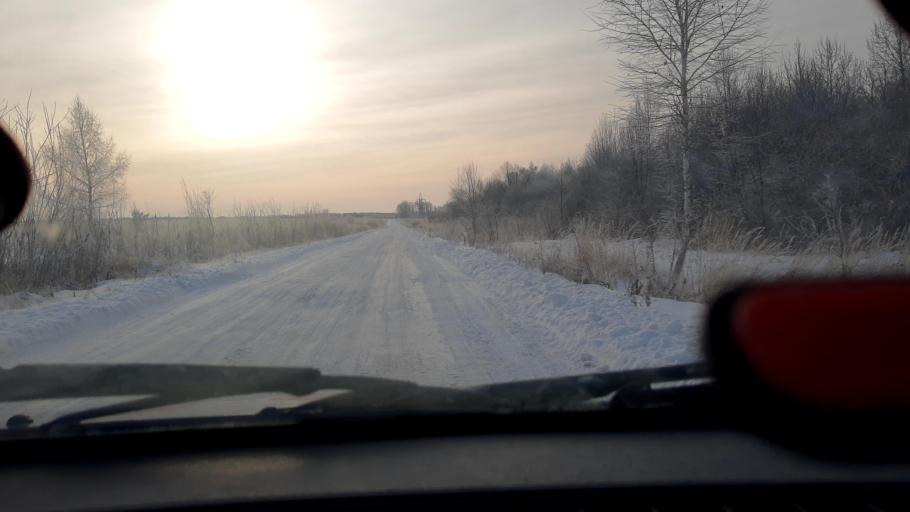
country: RU
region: Bashkortostan
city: Iglino
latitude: 54.7381
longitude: 56.2428
